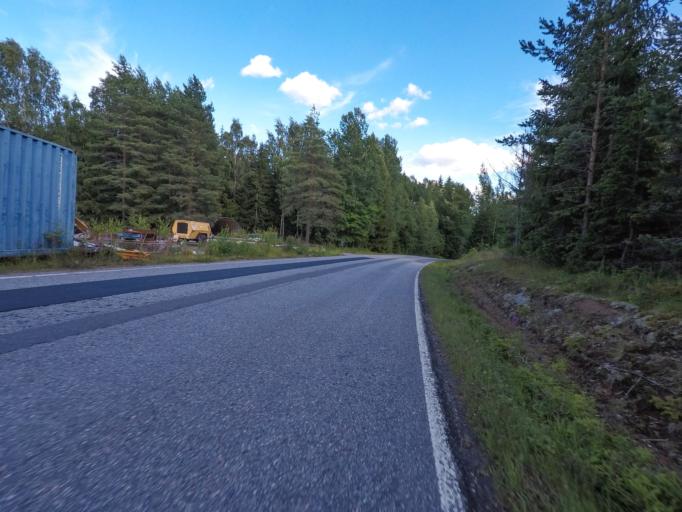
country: FI
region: South Karelia
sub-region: Imatra
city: Imatra
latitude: 61.1435
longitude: 28.6304
